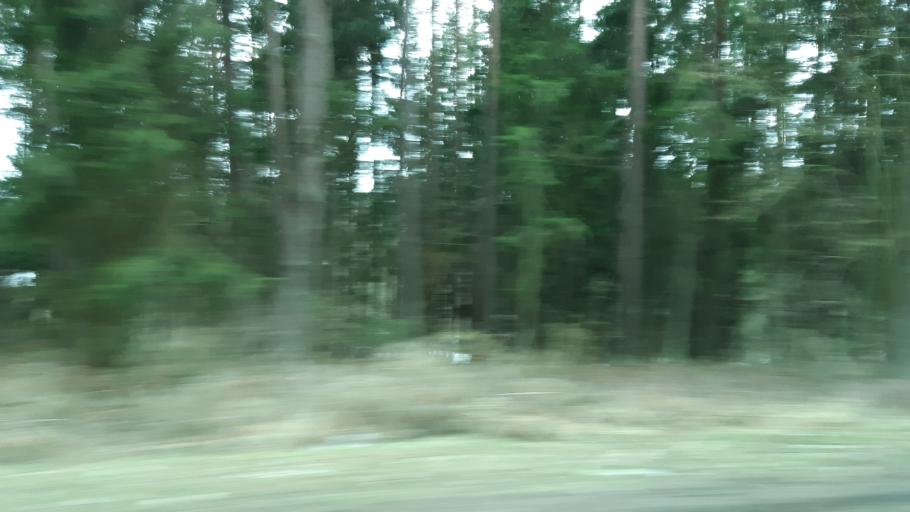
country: PL
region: Podlasie
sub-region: Suwalki
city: Suwalki
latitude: 54.3079
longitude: 22.9579
